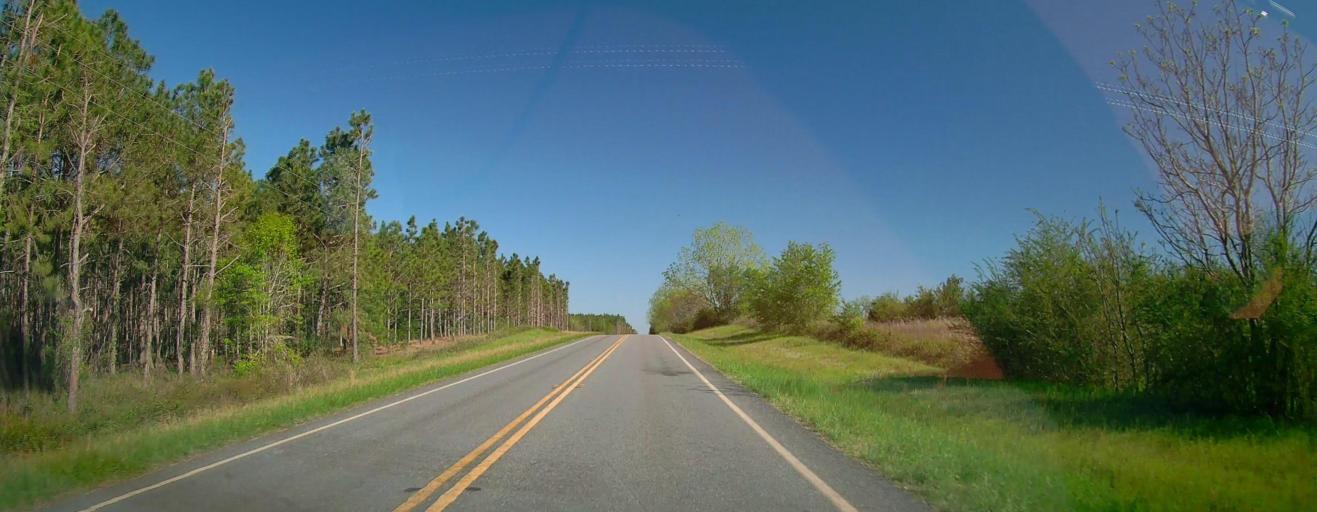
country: US
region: Georgia
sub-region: Wilcox County
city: Rochelle
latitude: 32.0005
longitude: -83.4795
